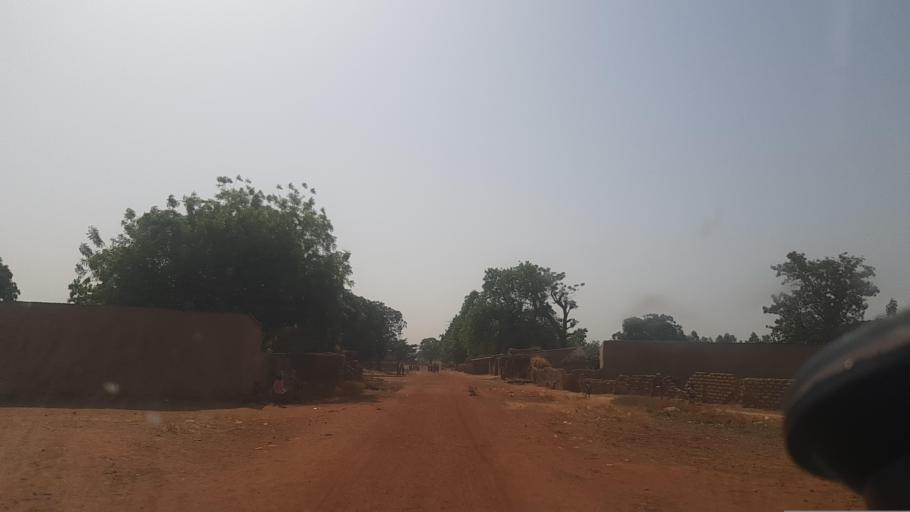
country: ML
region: Segou
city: Baroueli
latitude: 13.0127
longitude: -6.4227
